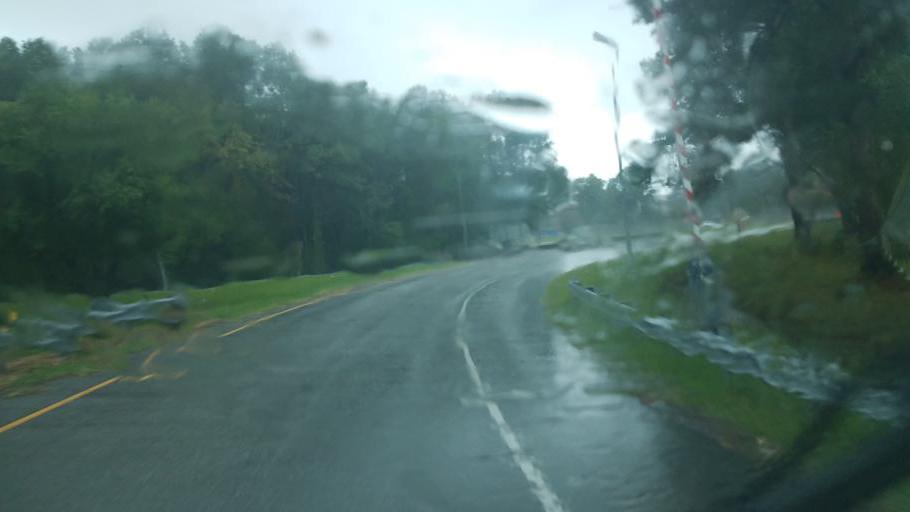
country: US
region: Virginia
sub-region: City of Poquoson
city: Poquoson
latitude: 37.0927
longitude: -76.4594
